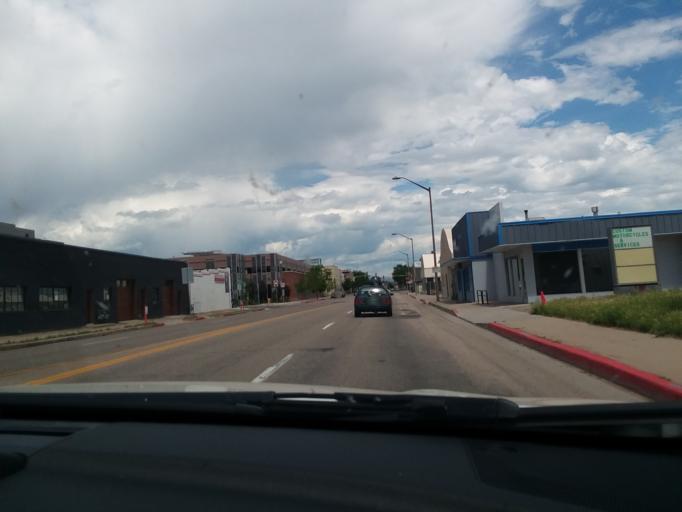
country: US
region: Colorado
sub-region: Larimer County
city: Fort Collins
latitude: 40.5877
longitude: -105.0721
